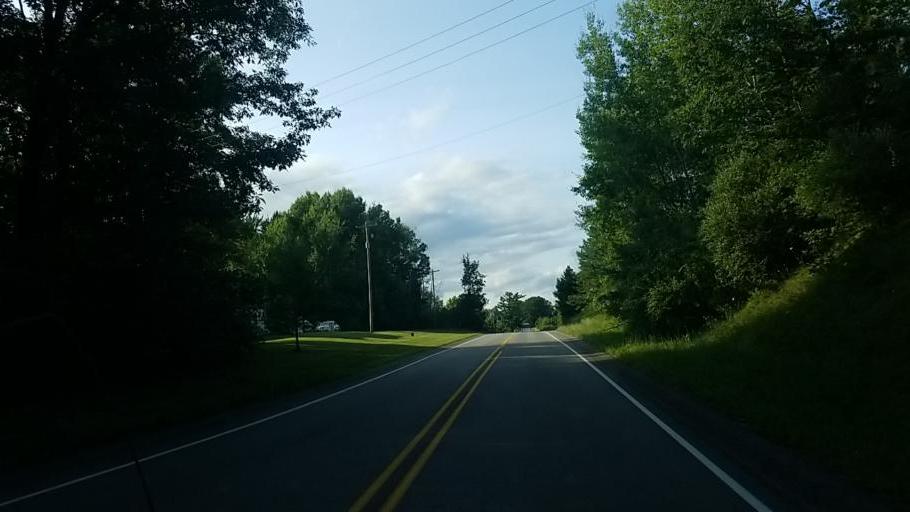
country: US
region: Michigan
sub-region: Montcalm County
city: Greenville
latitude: 43.2501
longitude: -85.3721
